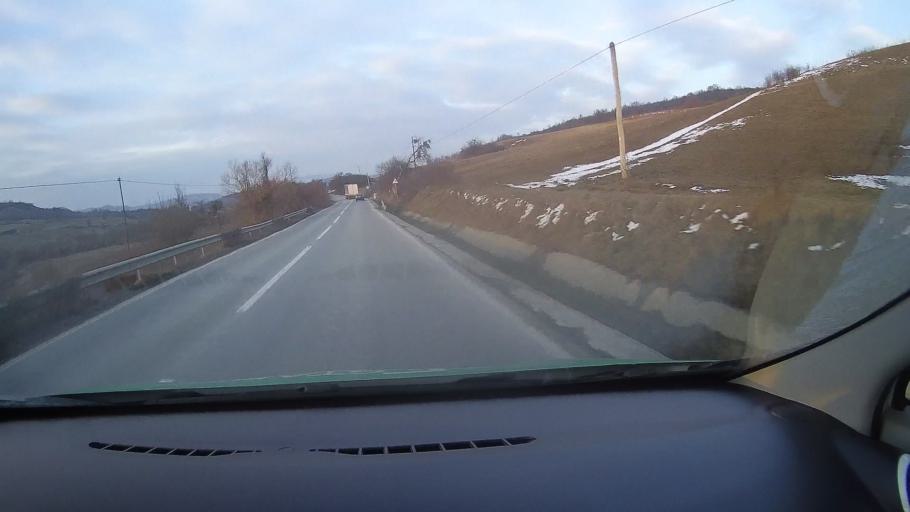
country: RO
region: Harghita
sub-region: Comuna Simonesti
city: Simonesti
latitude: 46.3240
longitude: 25.1012
